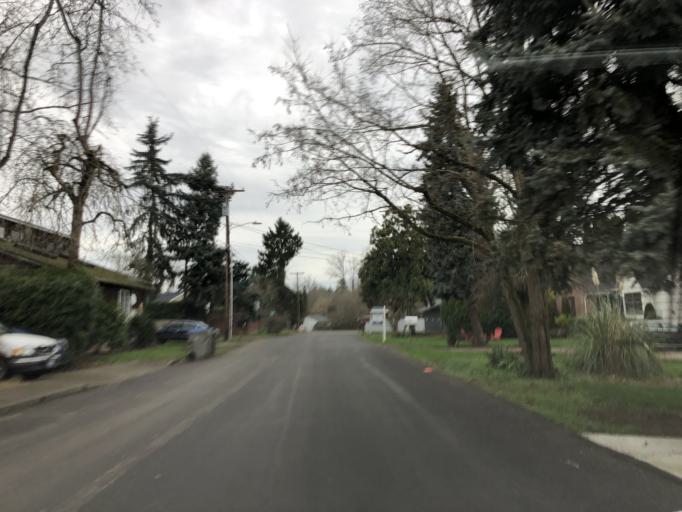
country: US
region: Oregon
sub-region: Washington County
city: Tigard
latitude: 45.4306
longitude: -122.7798
